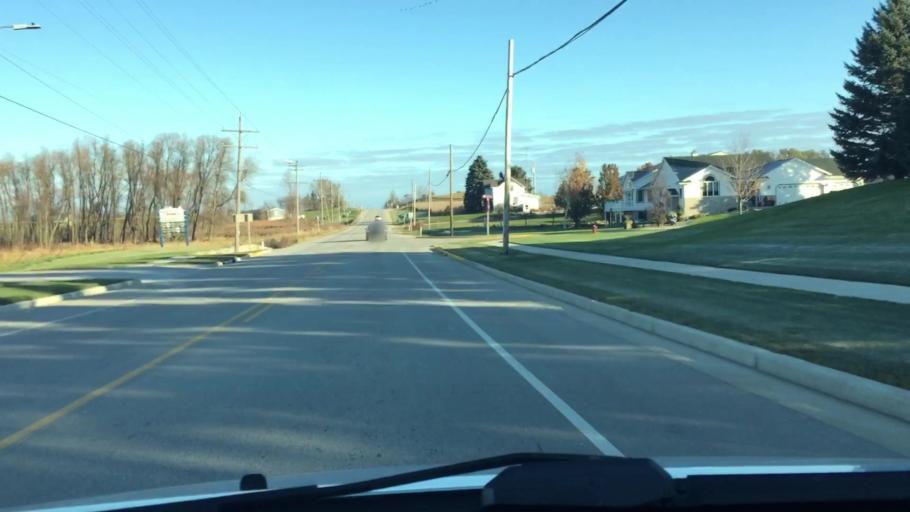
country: US
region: Wisconsin
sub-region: Dodge County
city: Lomira
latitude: 43.5969
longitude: -88.4502
